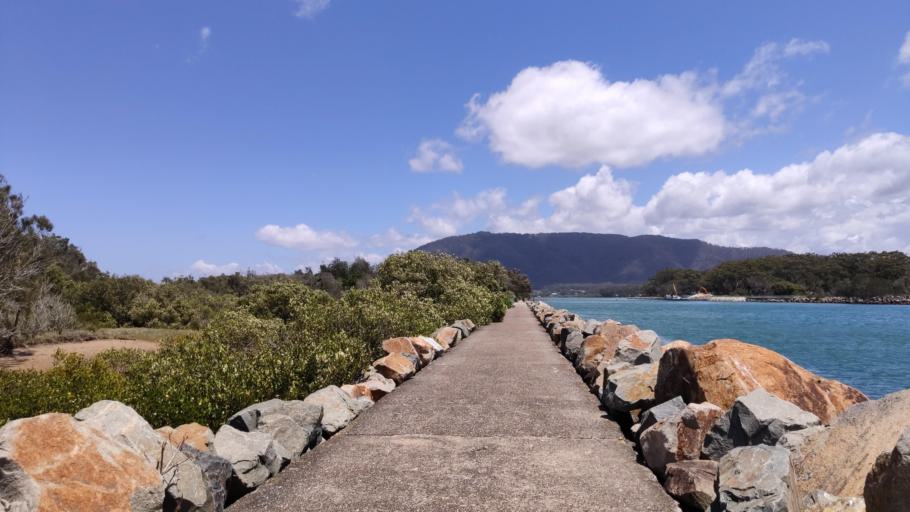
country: AU
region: New South Wales
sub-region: Port Macquarie-Hastings
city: North Haven
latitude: -31.6383
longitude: 152.8312
